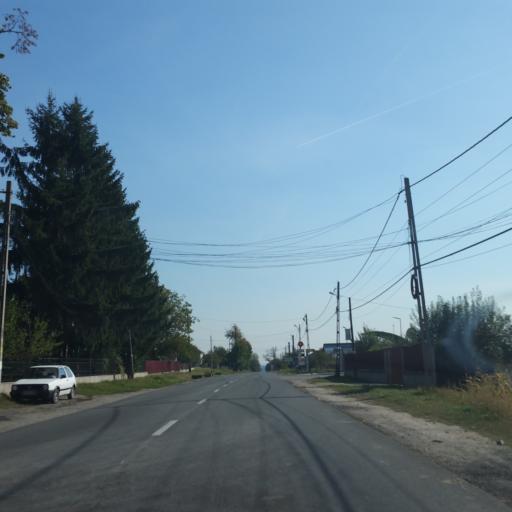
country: RO
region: Arges
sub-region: Comuna Baiculesti
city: Baiculesti
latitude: 45.0819
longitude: 24.6810
